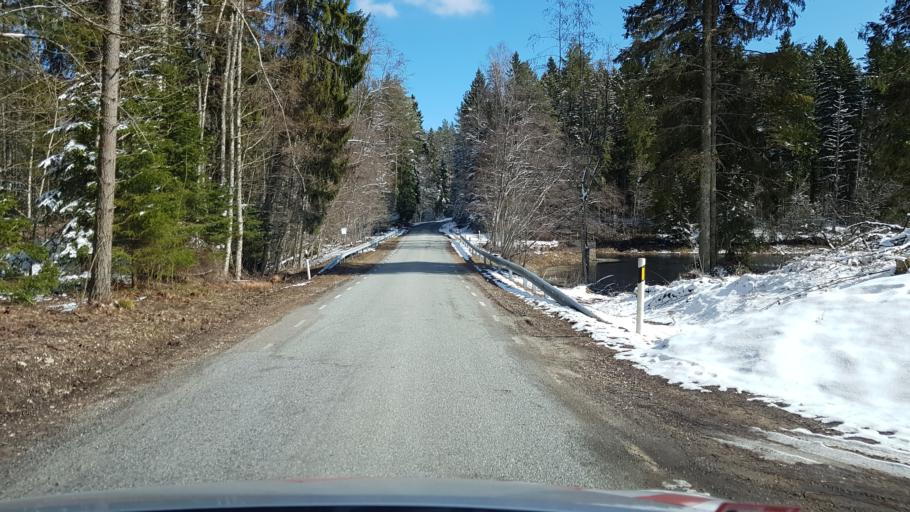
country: EE
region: Laeaene-Virumaa
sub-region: Tapa vald
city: Tapa
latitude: 59.5089
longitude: 25.9649
